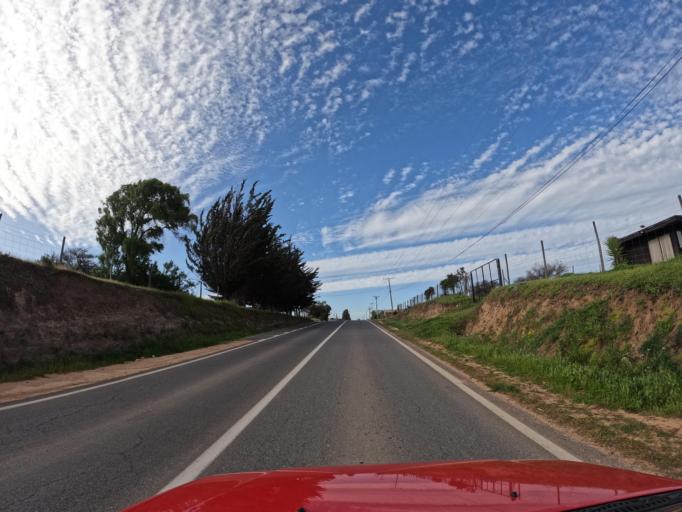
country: CL
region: Valparaiso
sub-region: San Antonio Province
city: San Antonio
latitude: -34.1450
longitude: -71.7313
